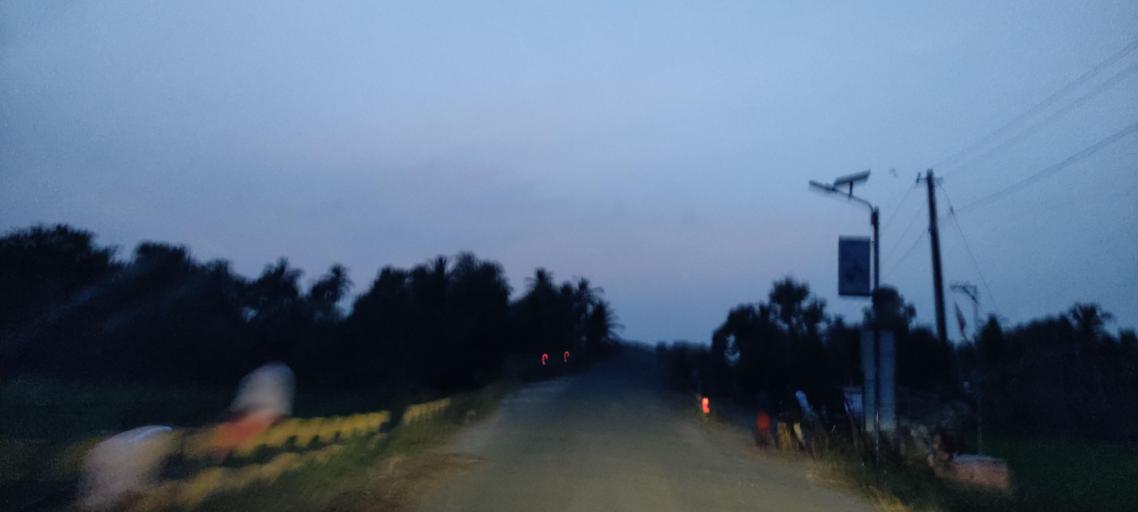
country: IN
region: Kerala
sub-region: Alappuzha
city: Mavelikara
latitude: 9.3204
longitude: 76.4362
